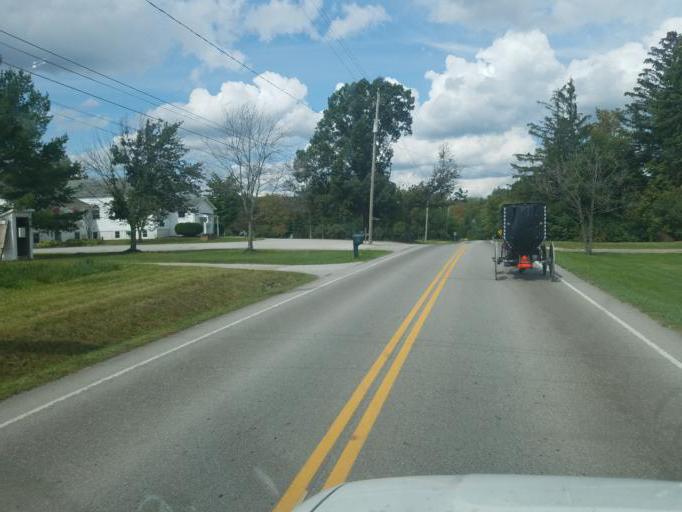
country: US
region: Ohio
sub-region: Geauga County
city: Middlefield
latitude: 41.4314
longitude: -81.0510
